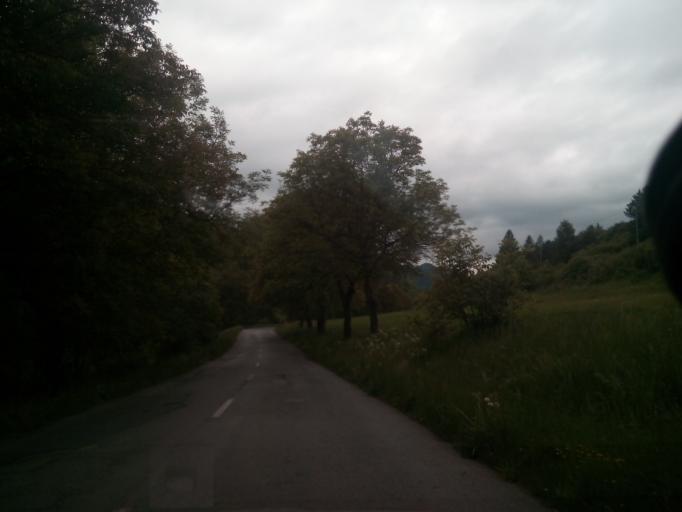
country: SK
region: Presovsky
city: Lipany
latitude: 49.0277
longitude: 20.9568
